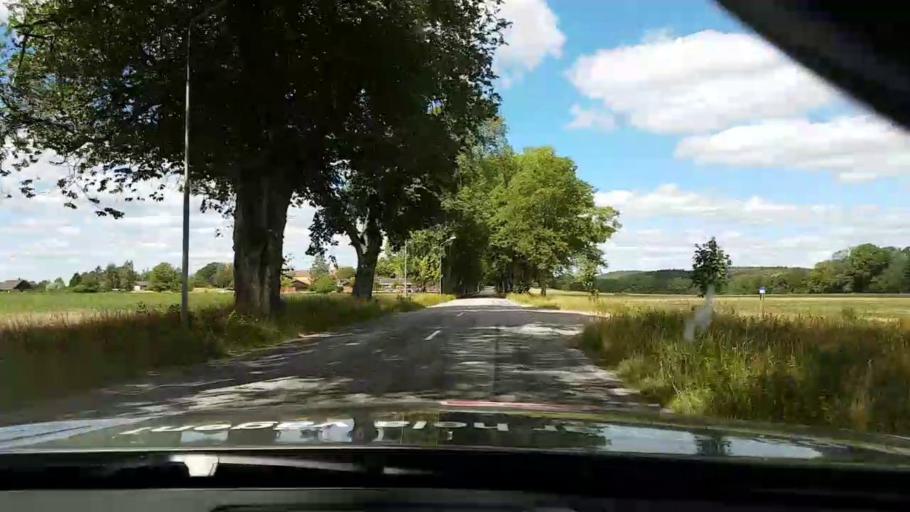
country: SE
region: Kalmar
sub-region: Vasterviks Kommun
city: Forserum
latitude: 58.0087
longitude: 16.4824
